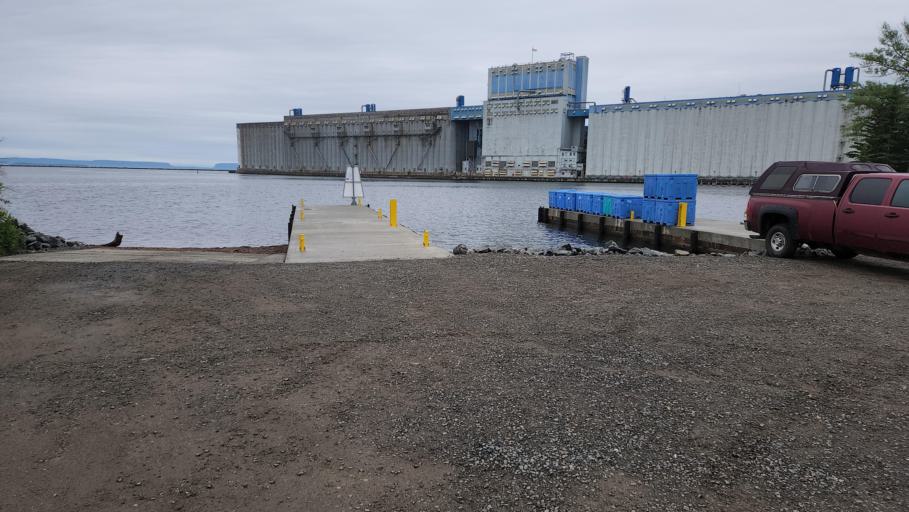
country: CA
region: Ontario
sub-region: Thunder Bay District
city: Thunder Bay
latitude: 48.4521
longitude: -89.1824
